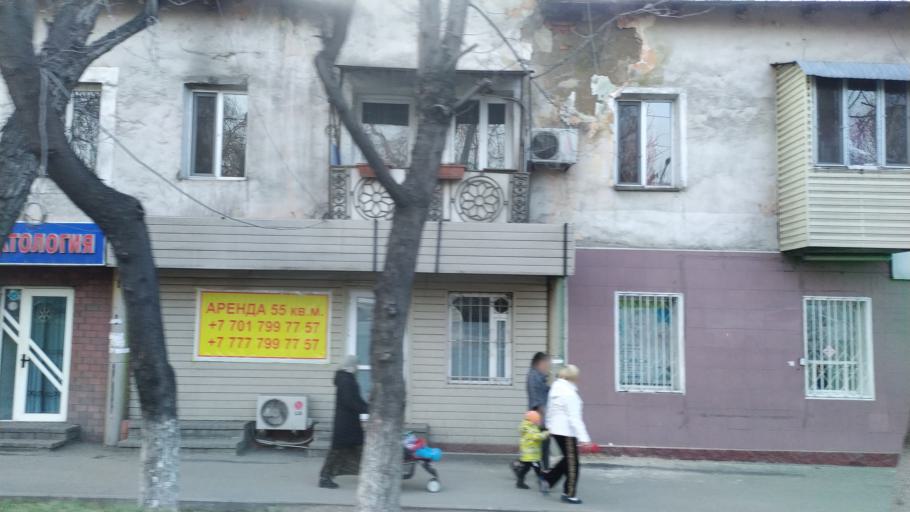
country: KZ
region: Almaty Qalasy
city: Almaty
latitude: 43.2225
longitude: 76.8845
